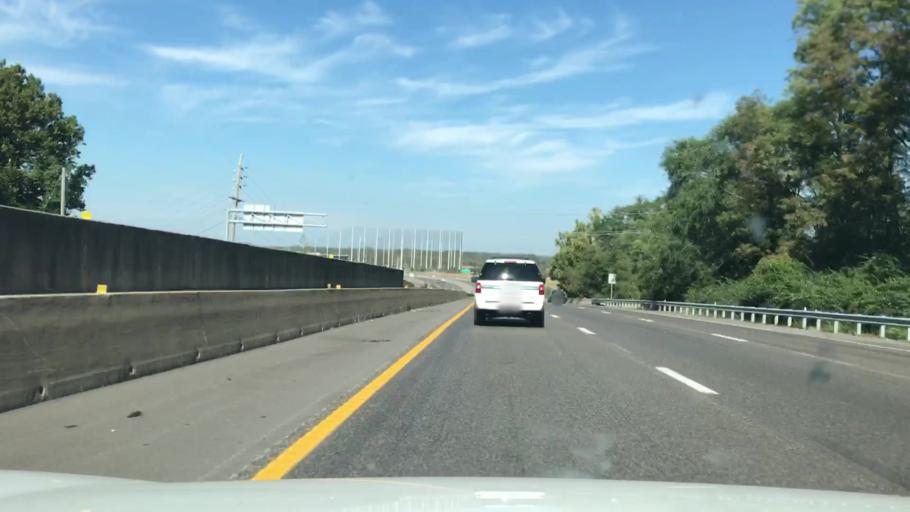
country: US
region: Missouri
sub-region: Saint Louis County
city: Chesterfield
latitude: 38.6640
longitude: -90.5719
